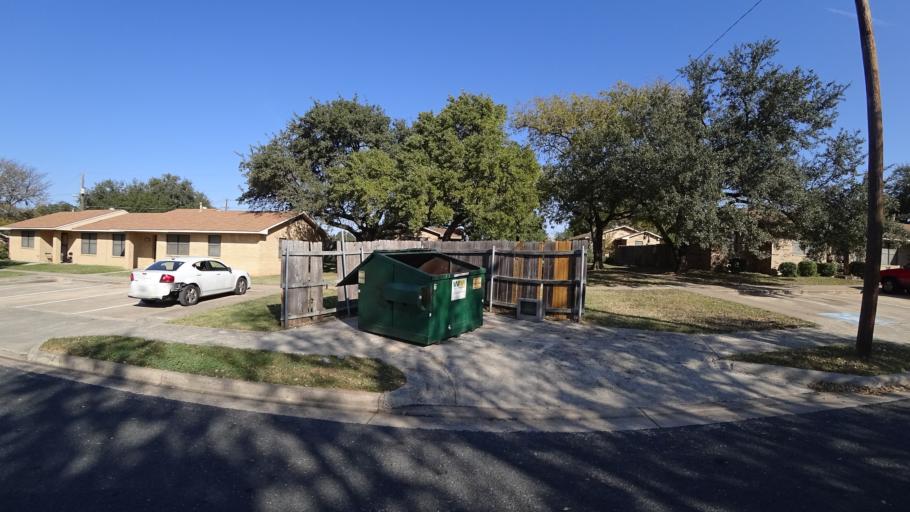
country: US
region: Texas
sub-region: Travis County
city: Barton Creek
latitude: 30.2336
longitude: -97.8514
